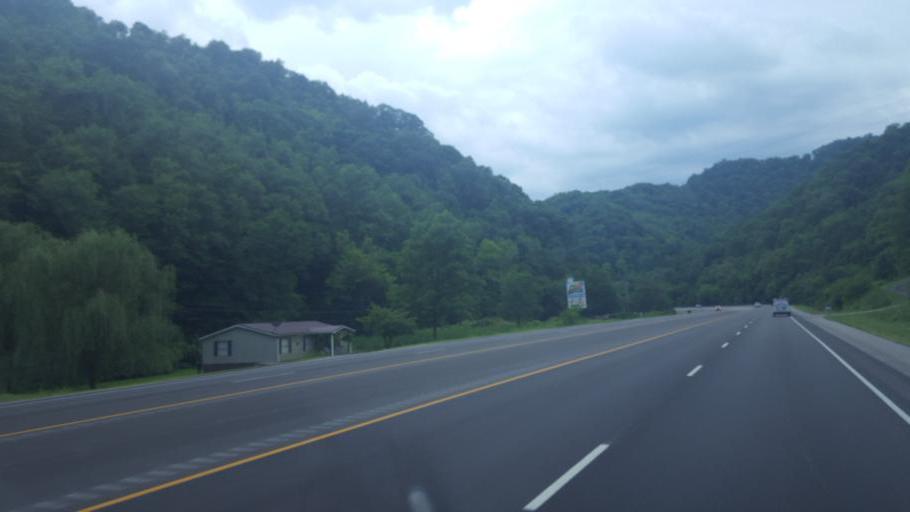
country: US
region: Kentucky
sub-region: Pike County
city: Pikeville
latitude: 37.3420
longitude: -82.5515
